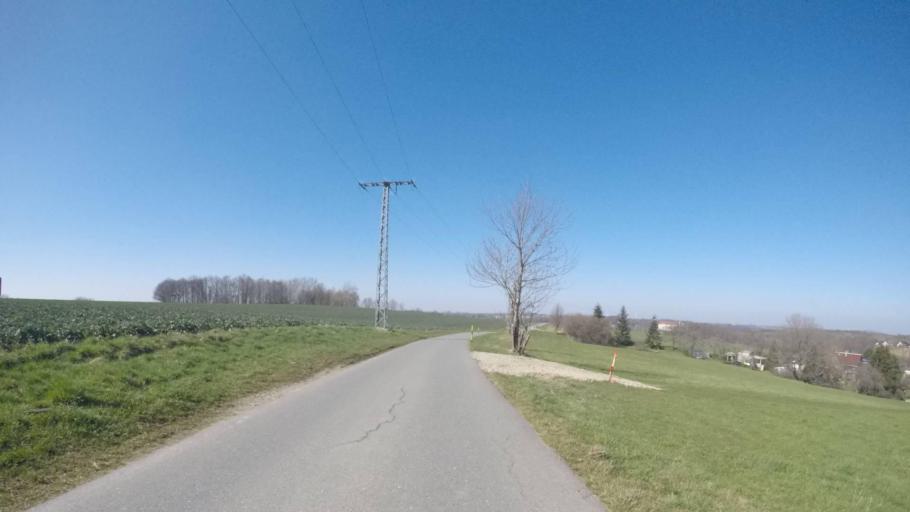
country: DE
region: Saxony
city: Niederfrohna
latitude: 50.8913
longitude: 12.6741
